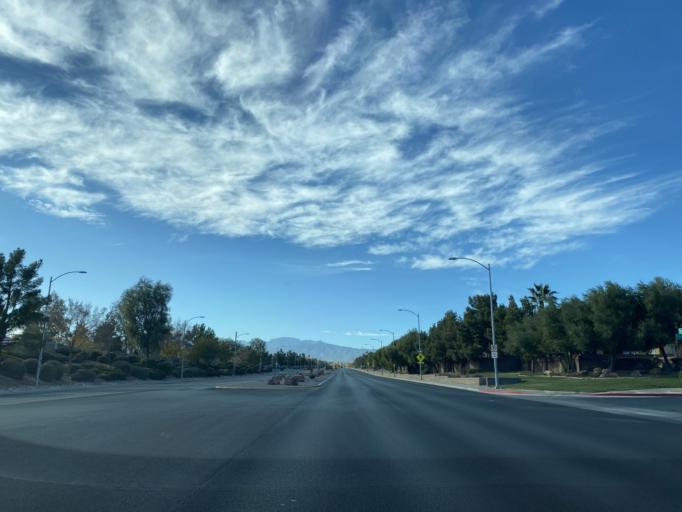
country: US
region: Nevada
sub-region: Clark County
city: North Las Vegas
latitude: 36.3054
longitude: -115.2623
